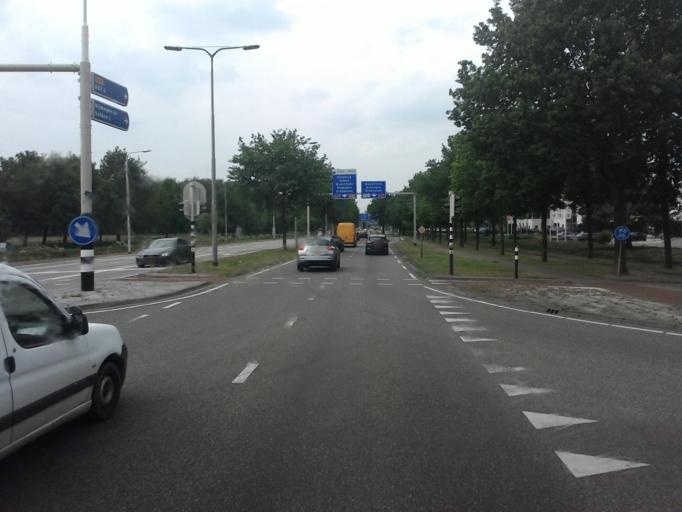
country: NL
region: Limburg
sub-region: Gemeente Venlo
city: Venlo
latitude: 51.3918
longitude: 6.1743
